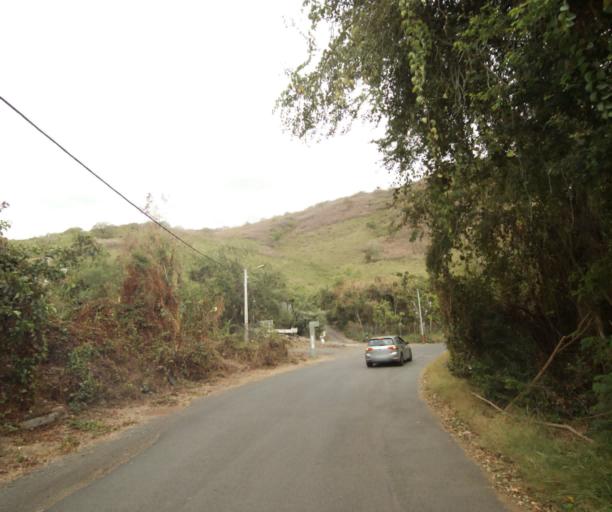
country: RE
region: Reunion
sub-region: Reunion
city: Saint-Paul
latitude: -21.0041
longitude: 55.3002
